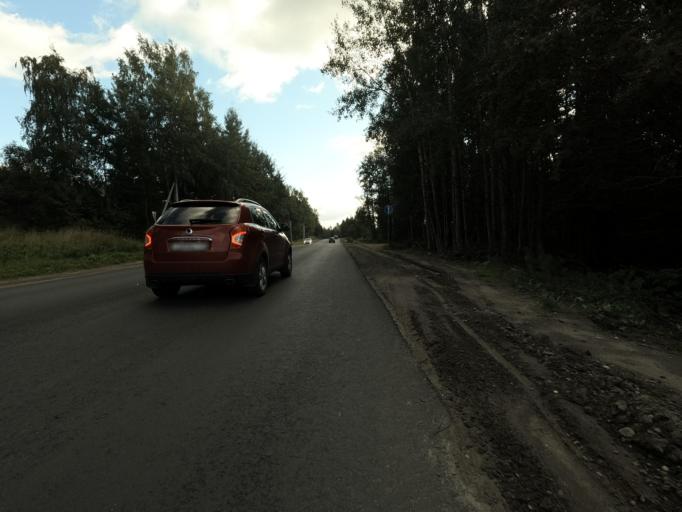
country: RU
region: Leningrad
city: Koltushi
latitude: 59.9740
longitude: 30.6533
